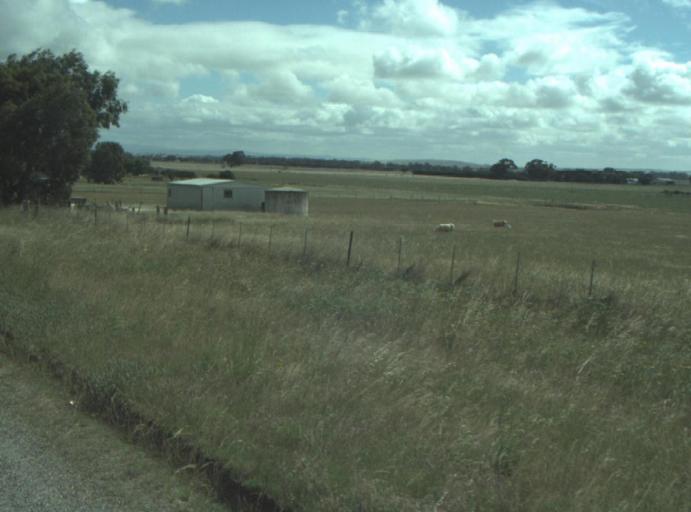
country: AU
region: Victoria
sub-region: Greater Geelong
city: Lara
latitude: -37.8620
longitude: 144.3249
